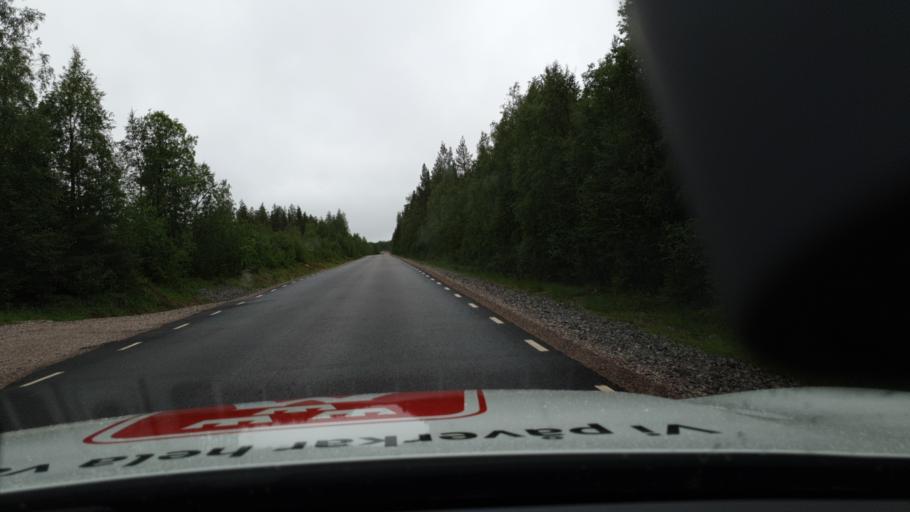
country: SE
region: Norrbotten
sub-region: Overtornea Kommun
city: OEvertornea
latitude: 66.4989
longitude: 23.4271
